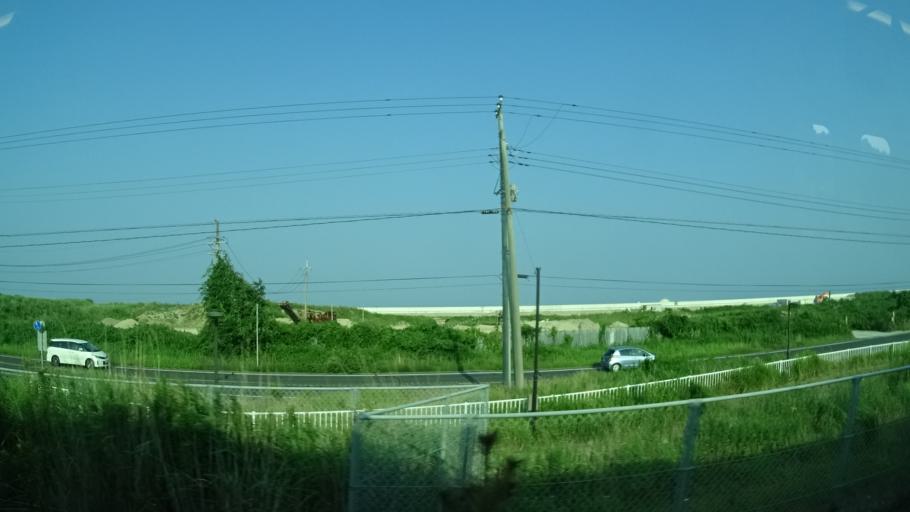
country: JP
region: Ibaraki
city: Takahagi
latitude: 36.6960
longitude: 140.7150
